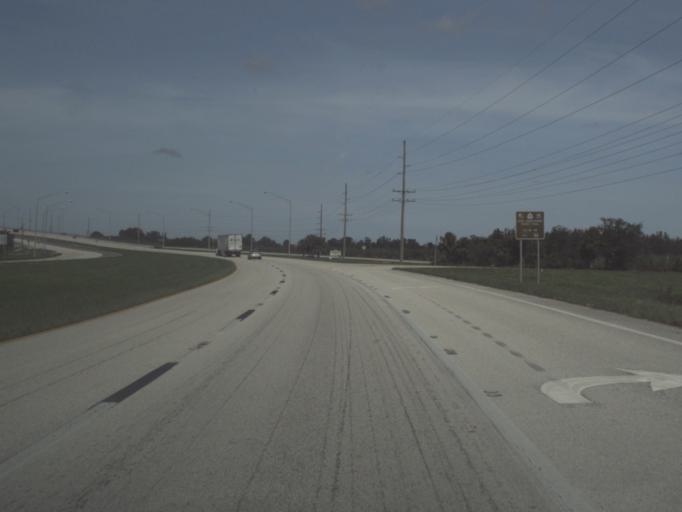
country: US
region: Florida
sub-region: Glades County
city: Moore Haven
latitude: 26.8281
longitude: -81.0824
